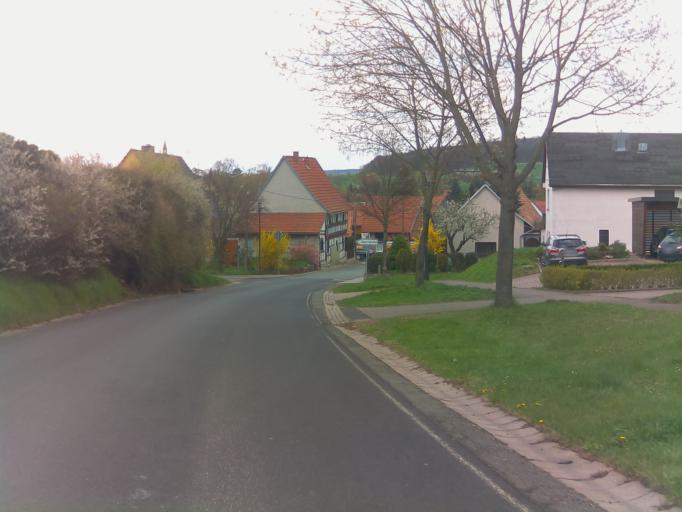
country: DE
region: Thuringia
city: Behringen
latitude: 50.7726
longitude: 11.0312
